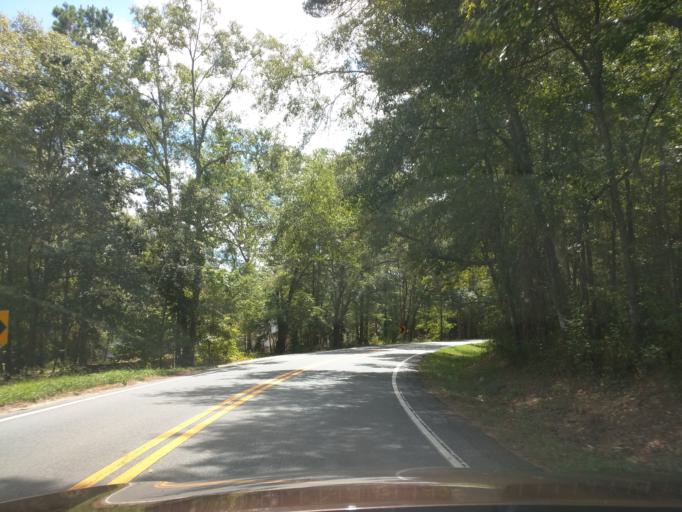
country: US
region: Florida
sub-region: Leon County
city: Tallahassee
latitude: 30.5363
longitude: -84.1320
